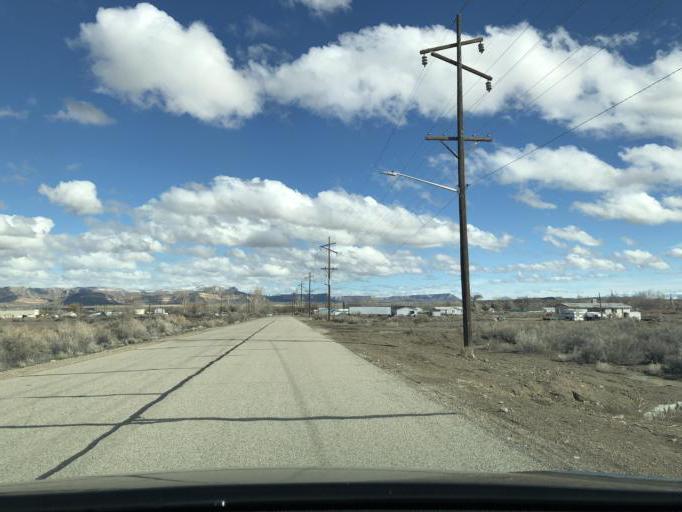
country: US
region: Utah
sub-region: Carbon County
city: East Carbon City
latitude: 39.0006
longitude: -110.1684
